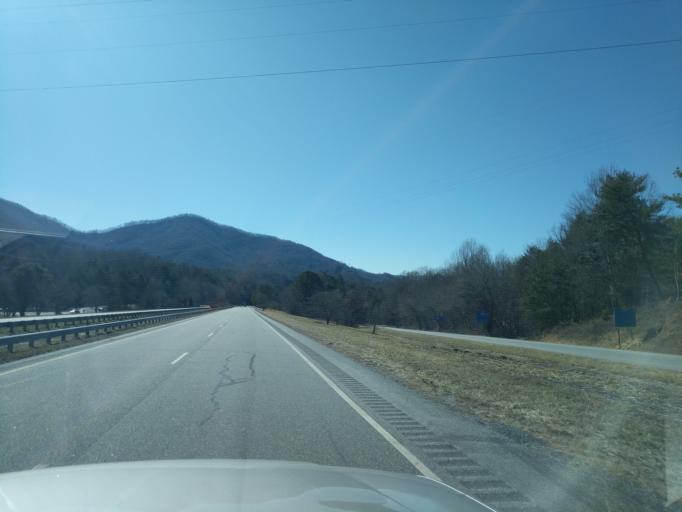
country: US
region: North Carolina
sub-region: Swain County
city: Bryson City
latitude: 35.4239
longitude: -83.4365
